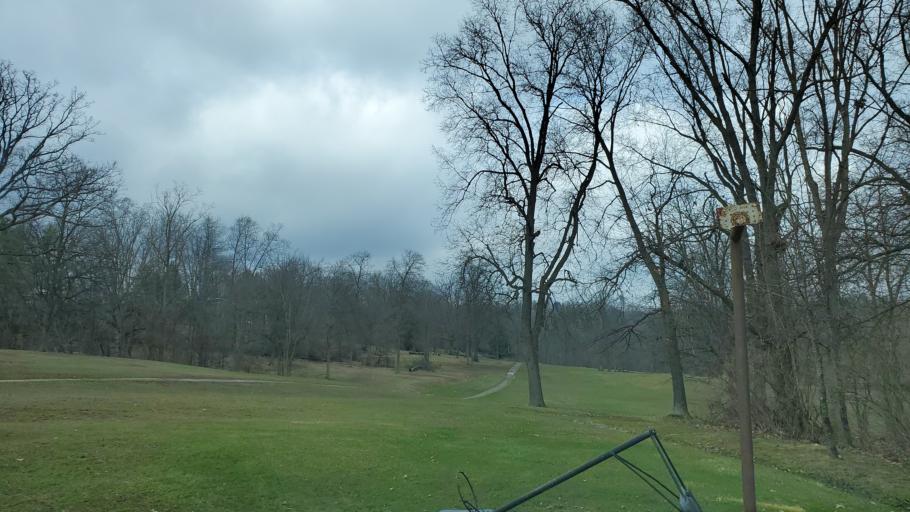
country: US
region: Ohio
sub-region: Licking County
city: Newark
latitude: 40.0268
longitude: -82.3804
